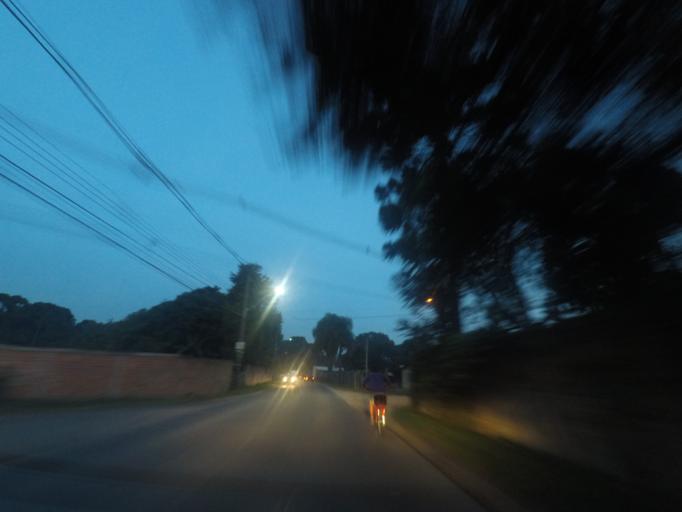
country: BR
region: Parana
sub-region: Pinhais
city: Pinhais
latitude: -25.4650
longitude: -49.1499
